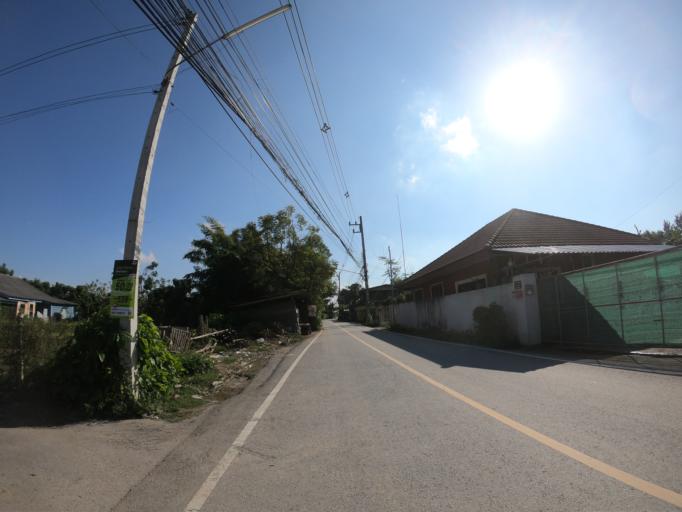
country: TH
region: Chiang Mai
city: Saraphi
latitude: 18.7156
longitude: 99.0022
